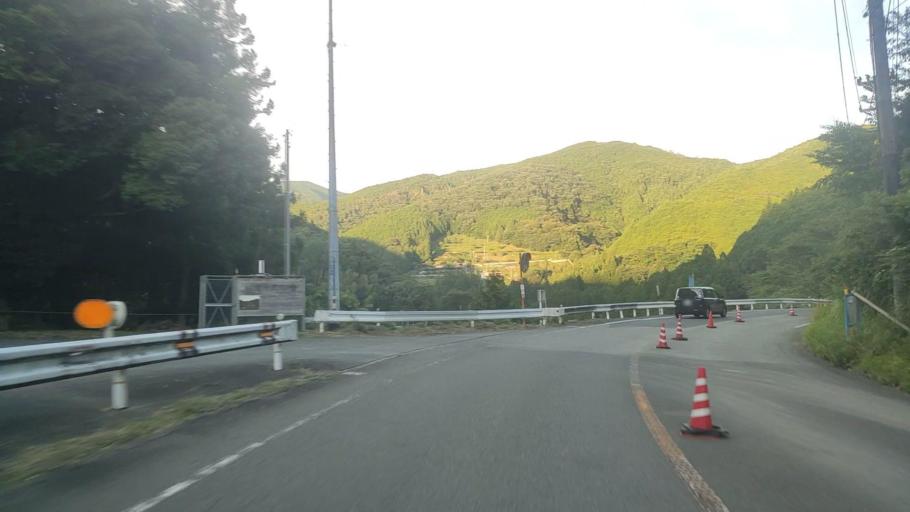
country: JP
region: Wakayama
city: Tanabe
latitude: 33.8176
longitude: 135.5561
